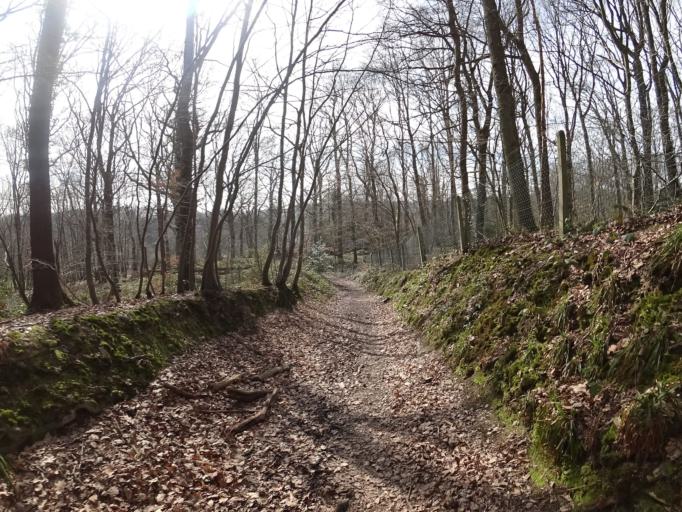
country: BE
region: Wallonia
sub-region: Province de Namur
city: Namur
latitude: 50.4403
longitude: 4.8379
